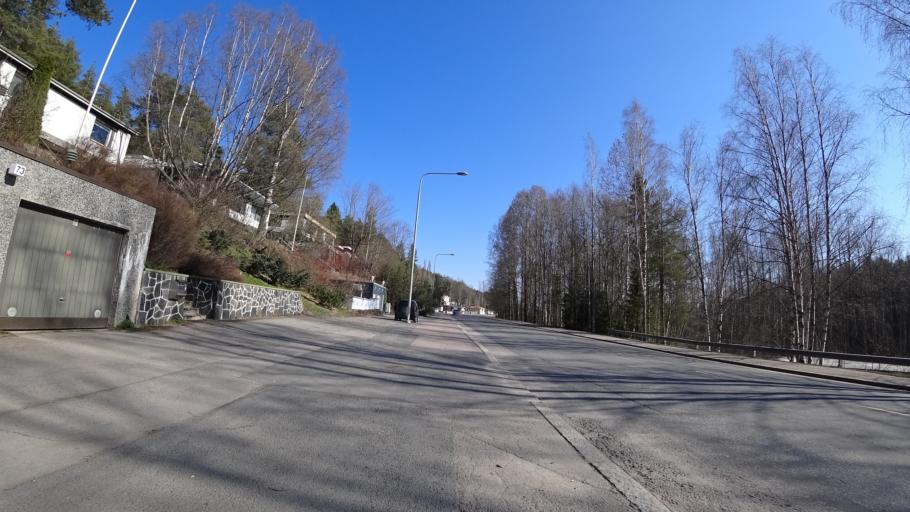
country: FI
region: Pirkanmaa
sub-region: Tampere
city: Pirkkala
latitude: 61.5180
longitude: 23.6464
